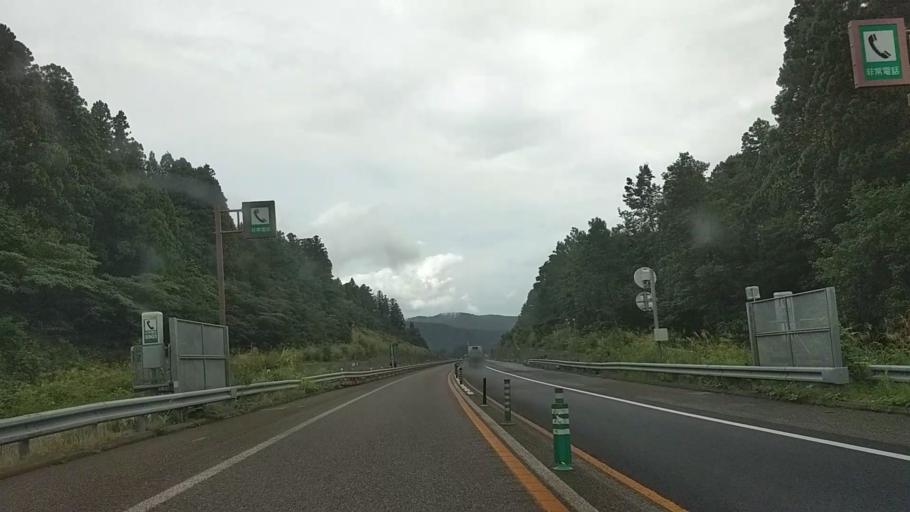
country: JP
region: Niigata
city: Arai
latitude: 36.9954
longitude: 138.2070
